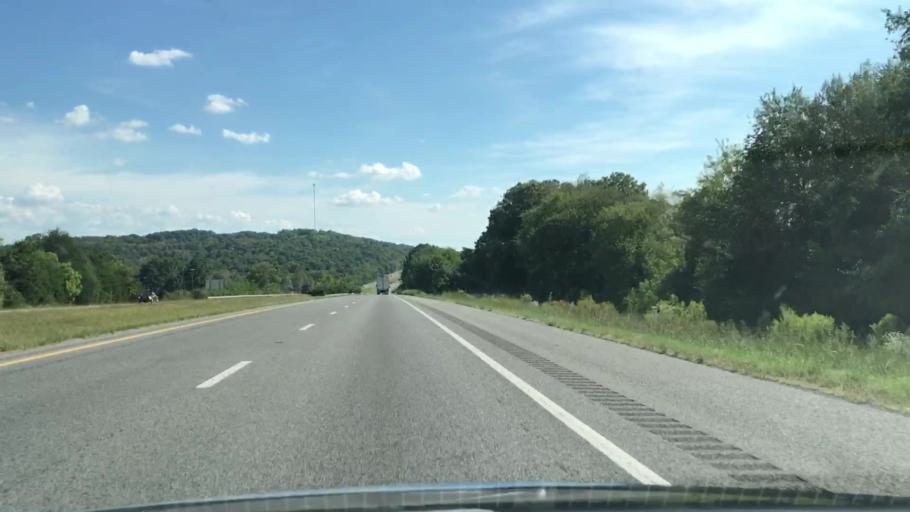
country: US
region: Alabama
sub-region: Limestone County
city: Ardmore
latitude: 35.0409
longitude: -86.8797
